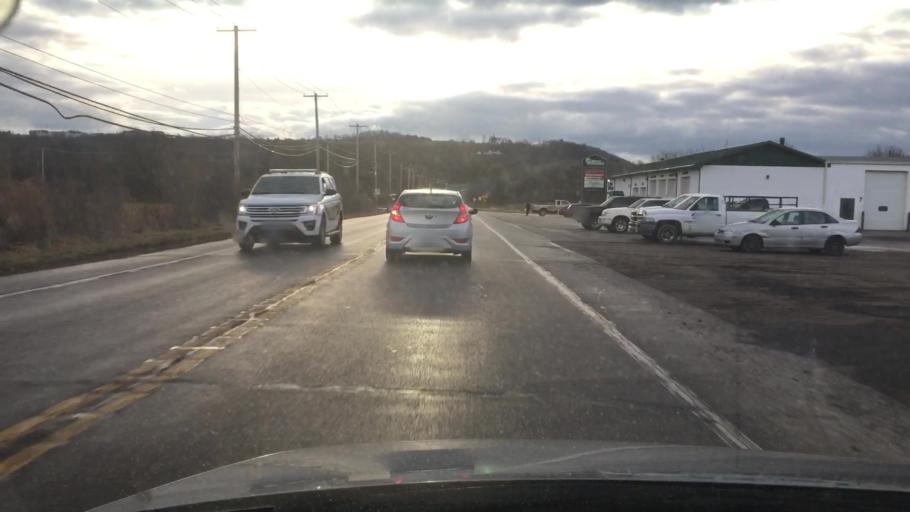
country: US
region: Pennsylvania
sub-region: Columbia County
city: Bloomsburg
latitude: 41.0250
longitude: -76.4777
